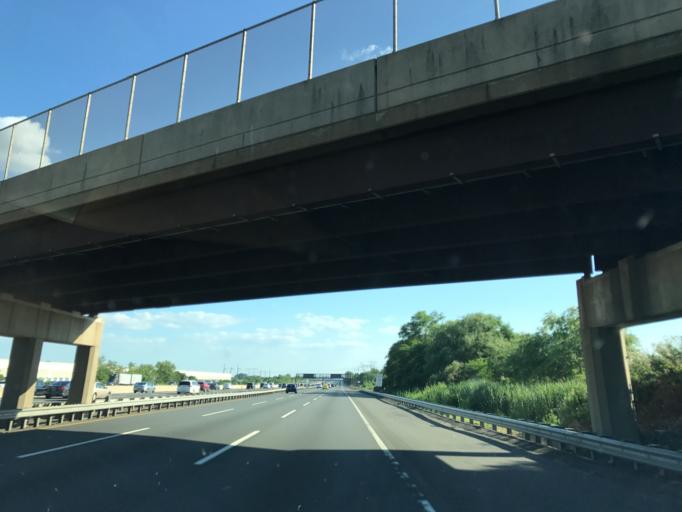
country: US
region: New Jersey
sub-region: Middlesex County
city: Helmetta
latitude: 40.3957
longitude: -74.4551
